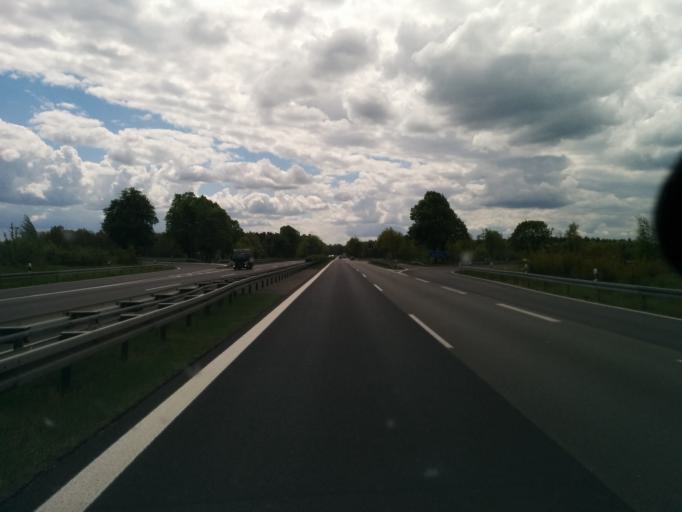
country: DE
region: Brandenburg
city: Werder
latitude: 52.4345
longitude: 12.9300
